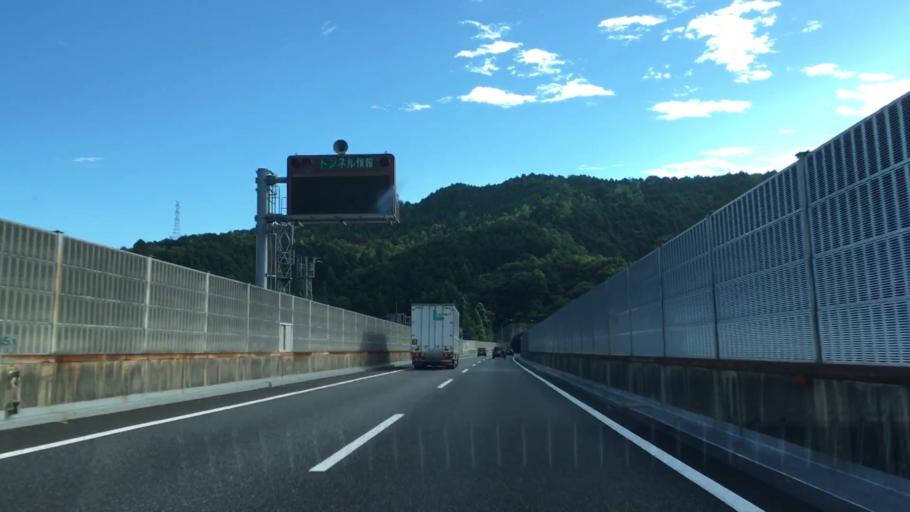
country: JP
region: Yamaguchi
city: Iwakuni
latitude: 34.1583
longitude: 132.1514
